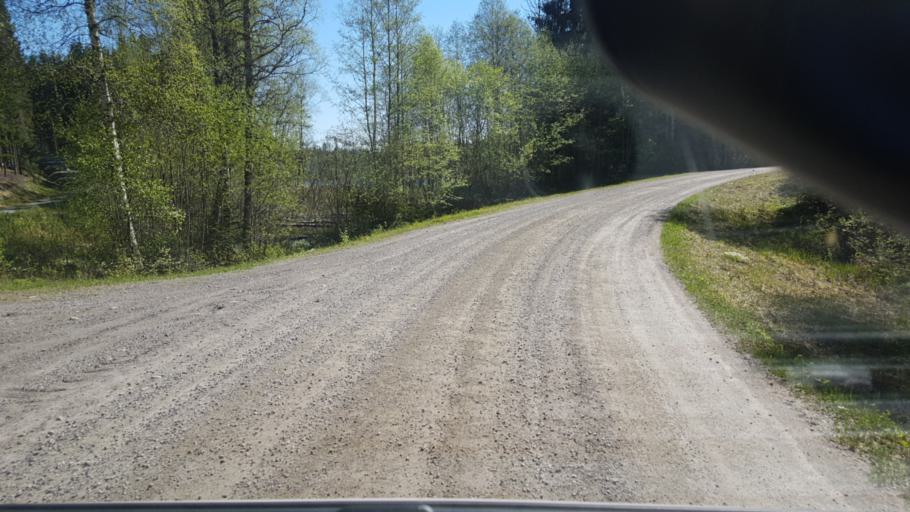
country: SE
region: Vaermland
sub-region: Eda Kommun
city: Charlottenberg
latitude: 59.9240
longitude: 12.3780
